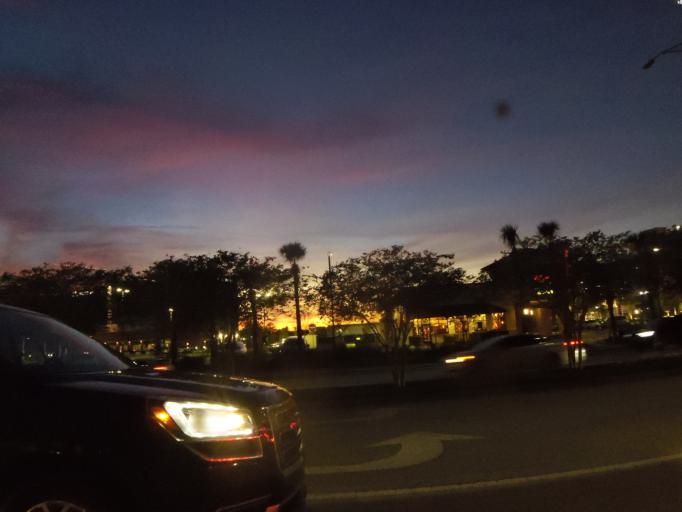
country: US
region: Florida
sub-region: Duval County
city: Jacksonville Beach
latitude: 30.2574
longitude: -81.5288
